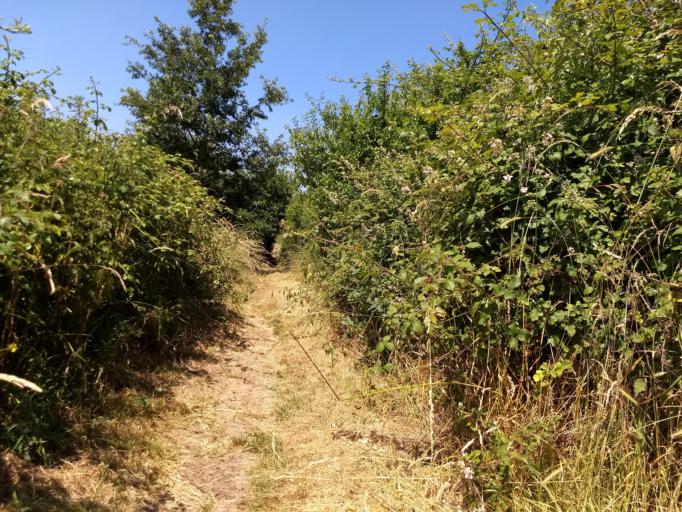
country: GB
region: England
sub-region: Isle of Wight
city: Newport
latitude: 50.7012
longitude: -1.3132
